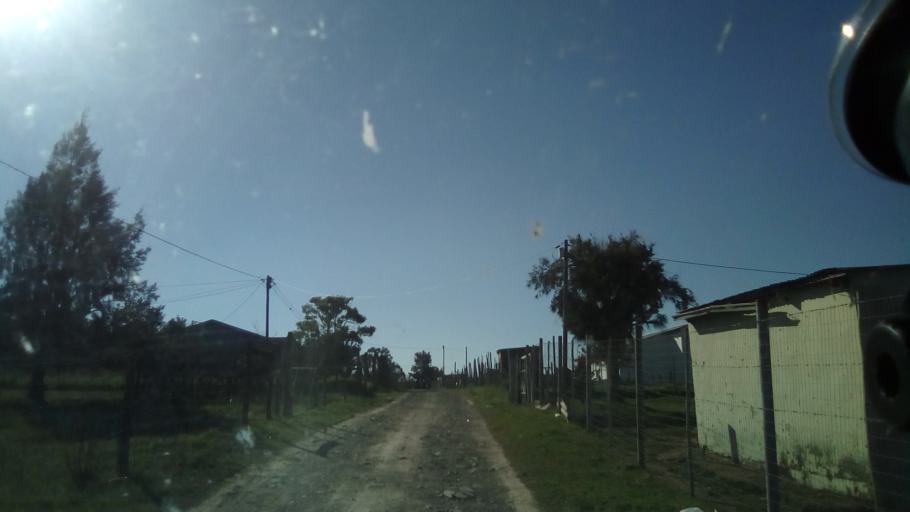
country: ZA
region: Eastern Cape
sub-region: Buffalo City Metropolitan Municipality
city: Bhisho
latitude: -32.8281
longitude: 27.3733
